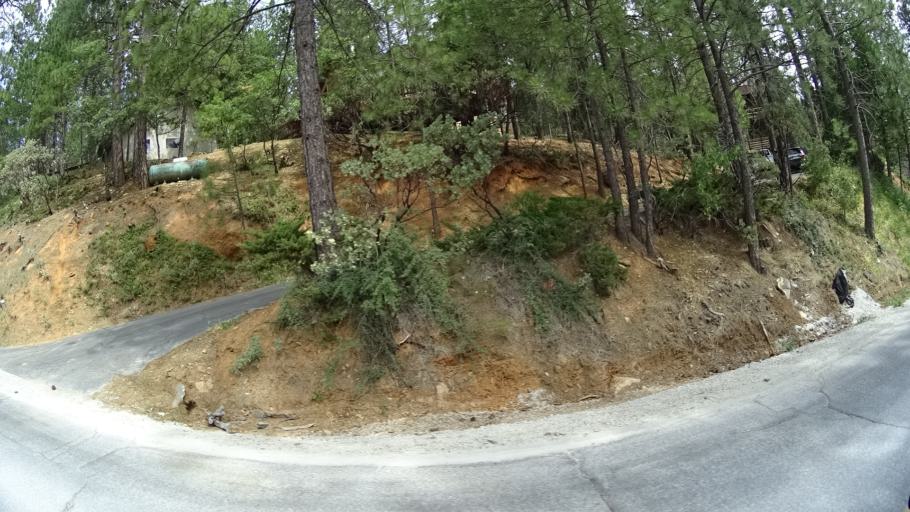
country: US
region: California
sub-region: Calaveras County
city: Arnold
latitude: 38.2436
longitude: -120.3414
